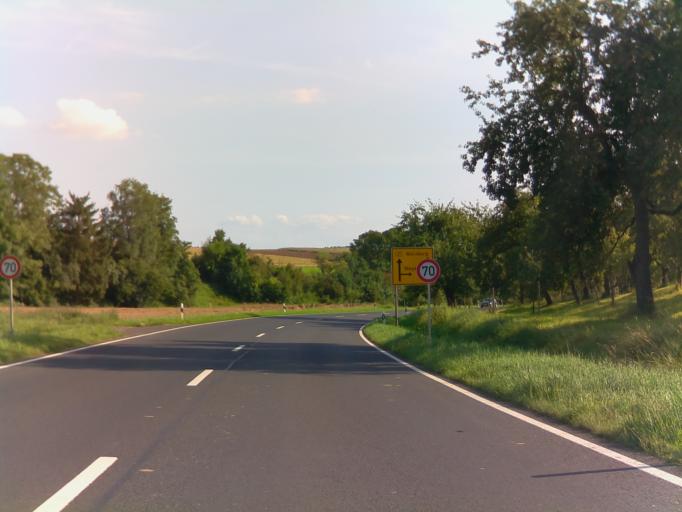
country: DE
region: Bavaria
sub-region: Regierungsbezirk Unterfranken
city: Karsbach
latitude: 50.0778
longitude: 9.7995
